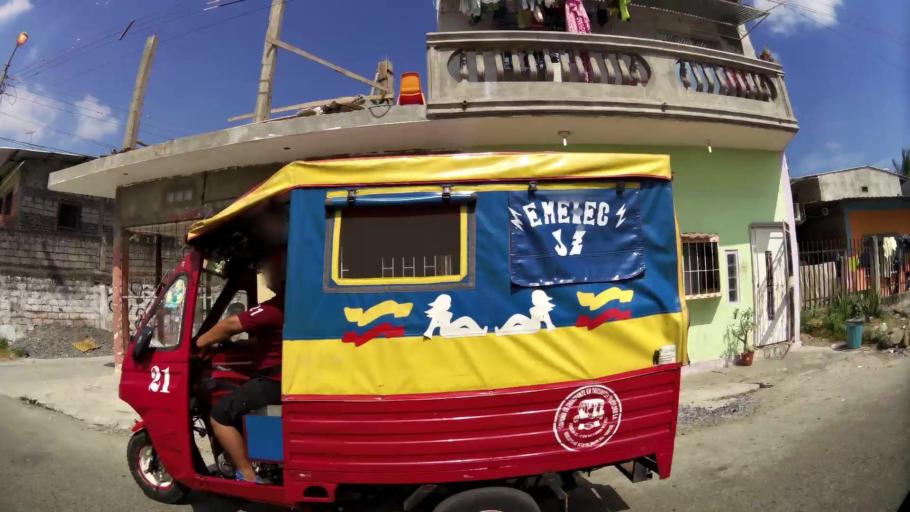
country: EC
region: Guayas
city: Santa Lucia
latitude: -2.1348
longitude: -79.9439
